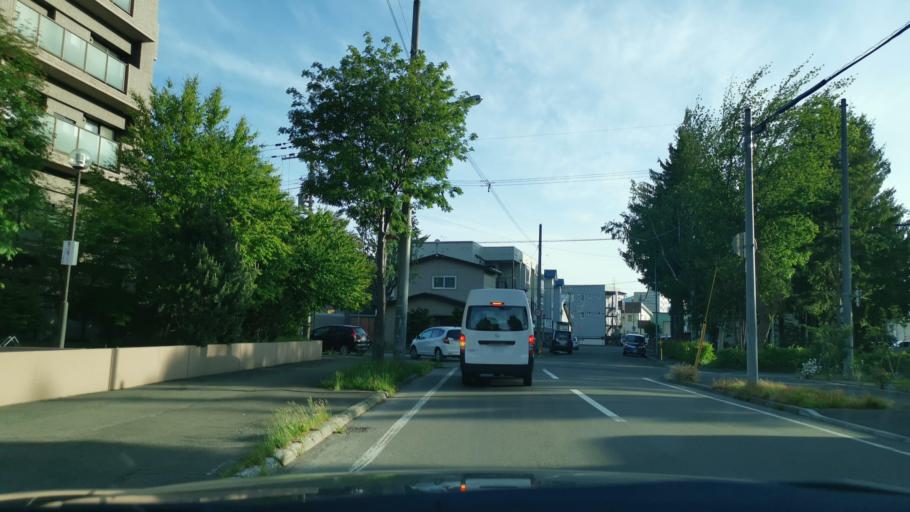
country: JP
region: Hokkaido
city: Sapporo
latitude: 43.0703
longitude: 141.4034
